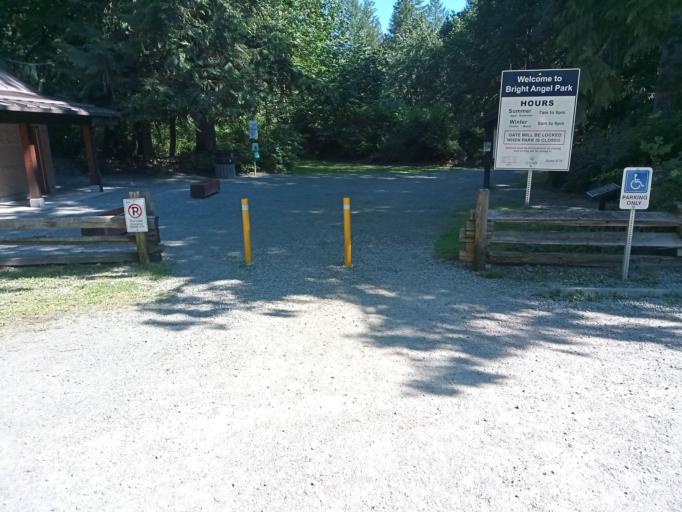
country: CA
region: British Columbia
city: Duncan
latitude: 48.7354
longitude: -123.6796
